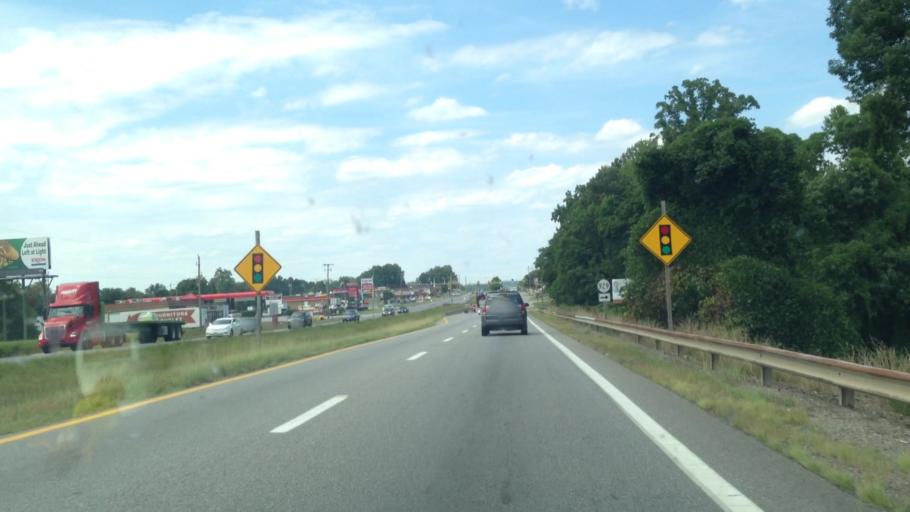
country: US
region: Virginia
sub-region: Henry County
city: Chatmoss
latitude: 36.5980
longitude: -79.8622
